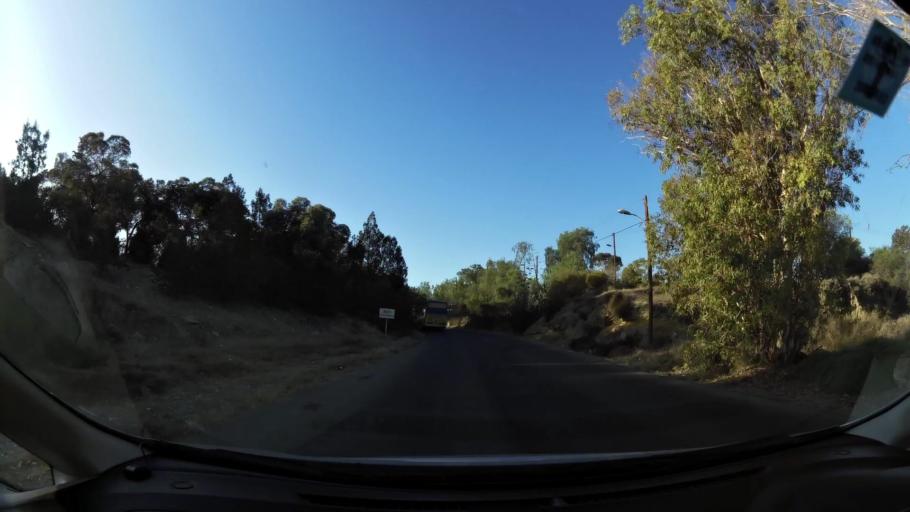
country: CY
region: Larnaka
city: Larnaca
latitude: 34.8971
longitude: 33.6328
